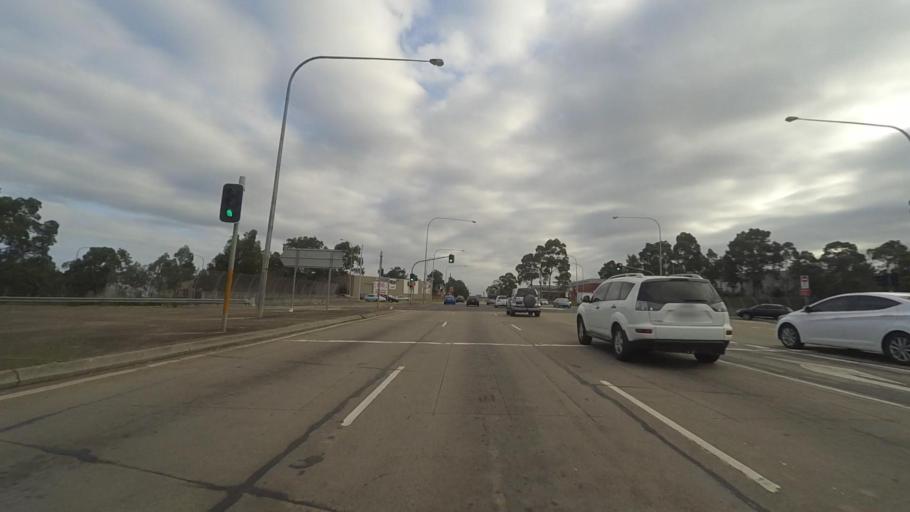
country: AU
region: New South Wales
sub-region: Bankstown
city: Padstow
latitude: -33.9399
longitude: 151.0358
